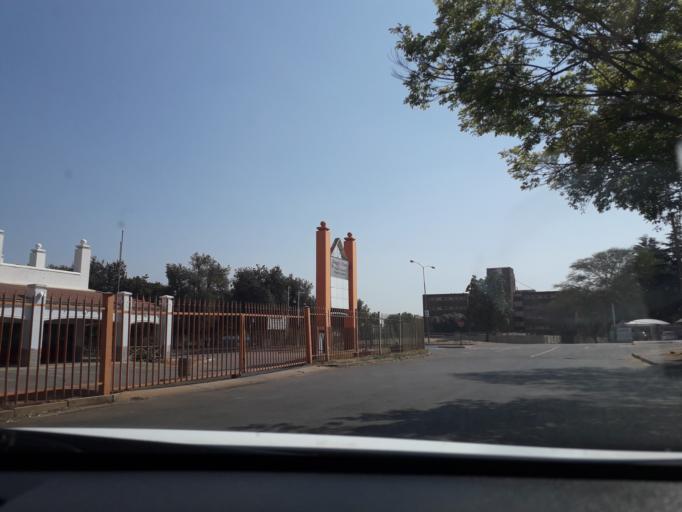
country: ZA
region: Gauteng
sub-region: City of Johannesburg Metropolitan Municipality
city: Modderfontein
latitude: -26.1026
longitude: 28.2297
